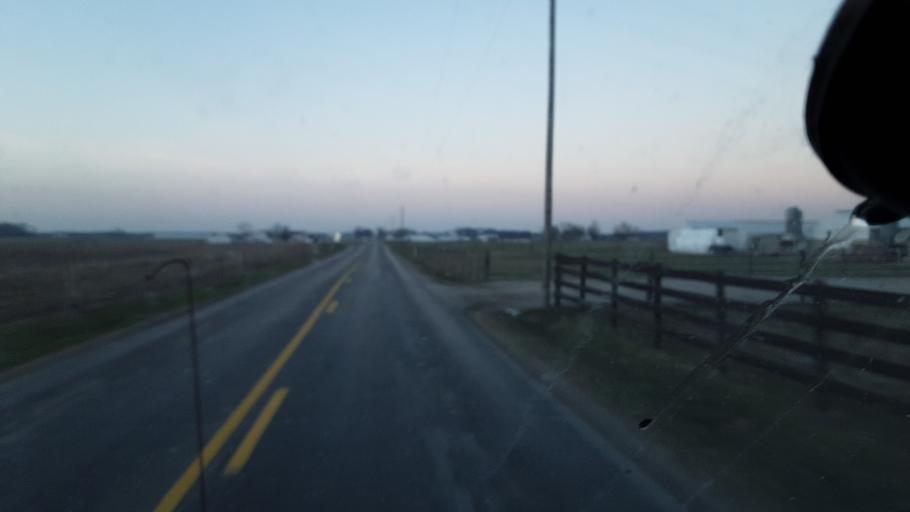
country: US
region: Indiana
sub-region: Allen County
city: Grabill
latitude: 41.2251
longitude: -84.9424
